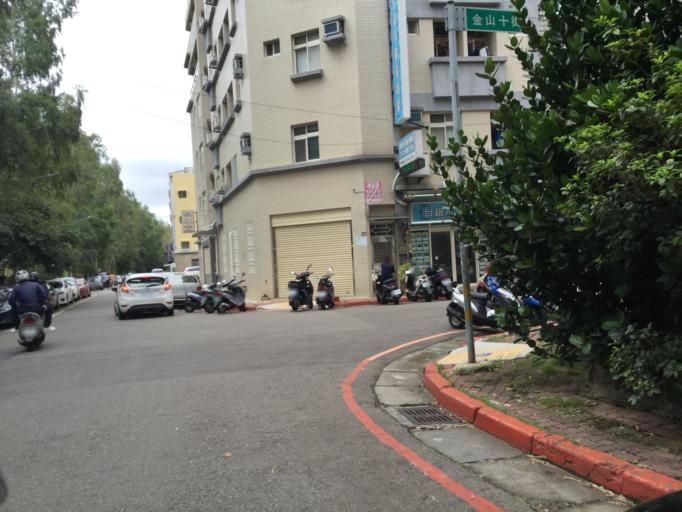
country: TW
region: Taiwan
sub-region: Hsinchu
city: Hsinchu
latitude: 24.7761
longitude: 121.0217
